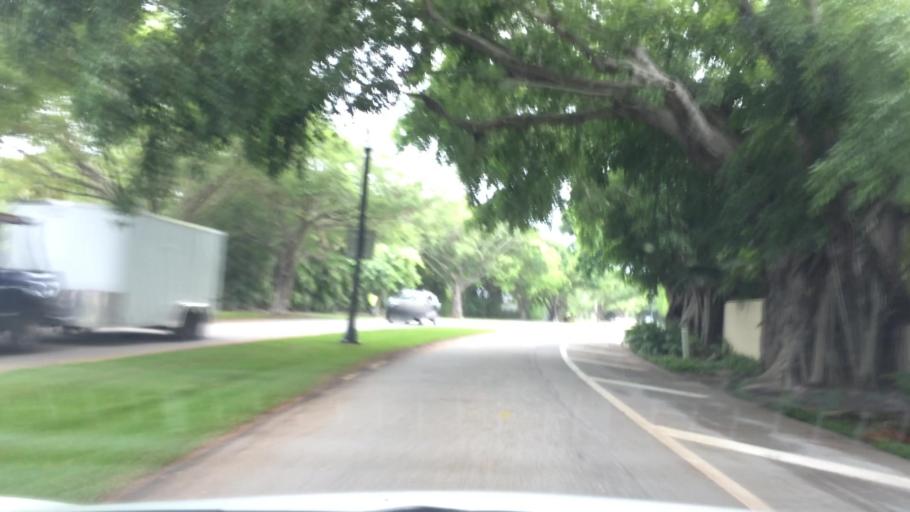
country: US
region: Florida
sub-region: Palm Beach County
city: West Palm Beach
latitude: 26.7263
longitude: -80.0380
